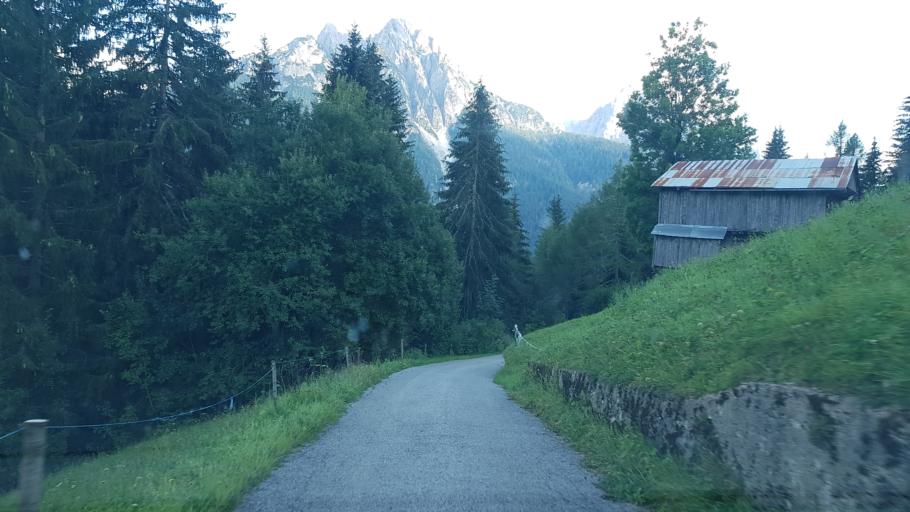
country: IT
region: Veneto
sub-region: Provincia di Belluno
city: San Pietro di Cadore
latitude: 46.5848
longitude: 12.5931
